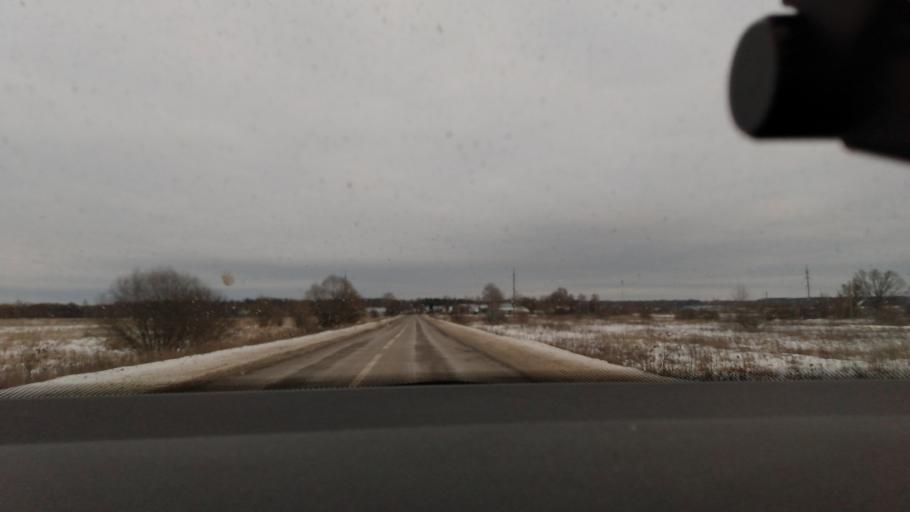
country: RU
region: Moskovskaya
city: Krasnaya Poyma
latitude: 55.1664
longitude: 39.1956
